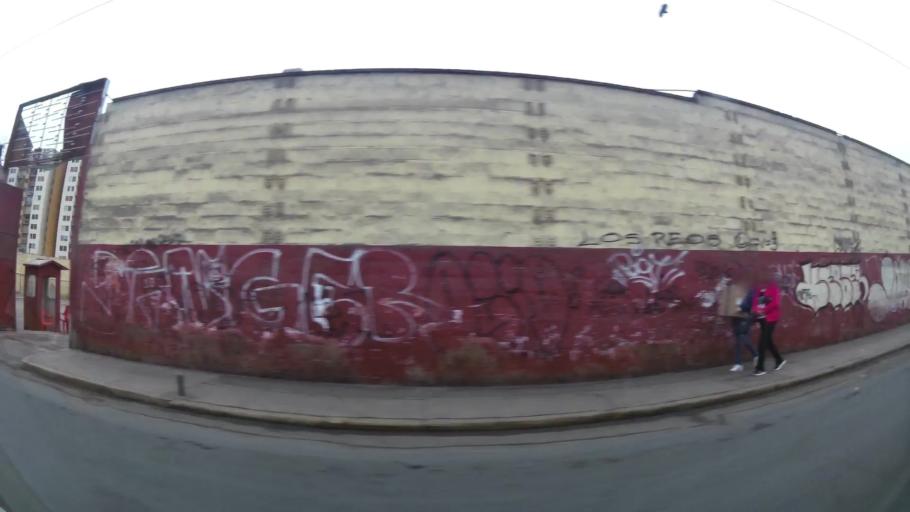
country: PE
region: Lima
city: Lima
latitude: -12.0501
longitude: -77.0484
